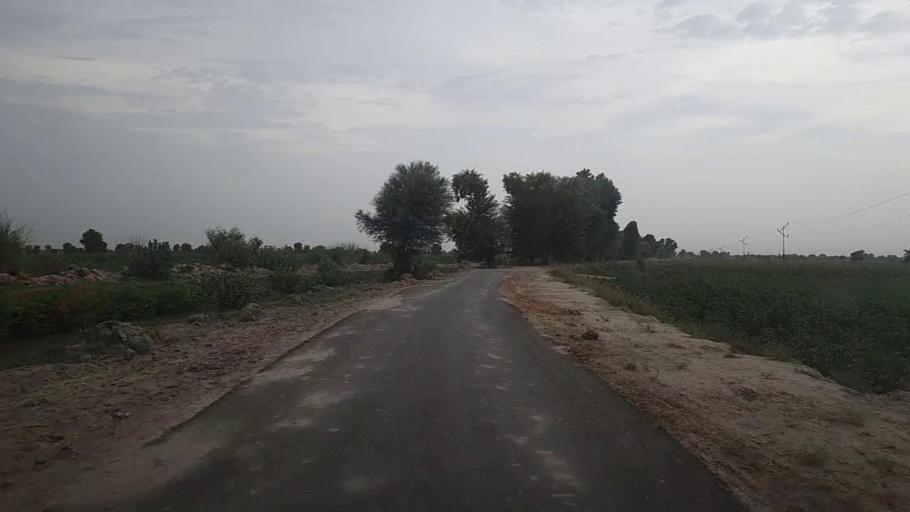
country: PK
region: Sindh
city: Karaundi
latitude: 26.9614
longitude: 68.3658
